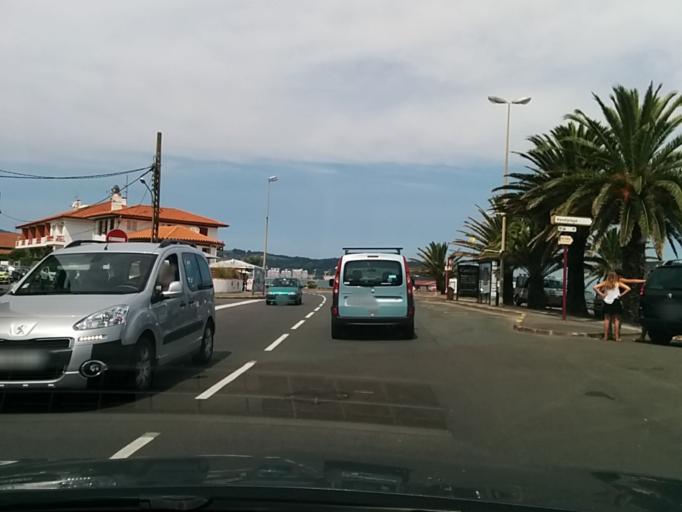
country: FR
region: Aquitaine
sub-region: Departement des Pyrenees-Atlantiques
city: Hendaye
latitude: 43.3755
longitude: -1.7618
